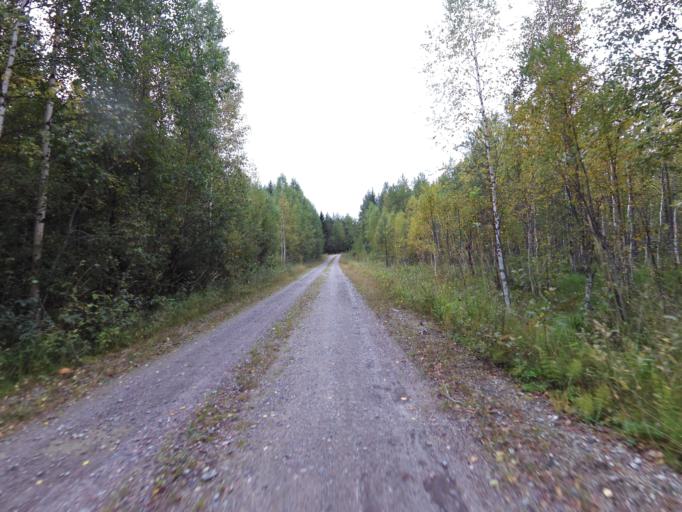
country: SE
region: Gaevleborg
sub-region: Gavle Kommun
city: Valbo
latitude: 60.7447
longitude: 17.0151
